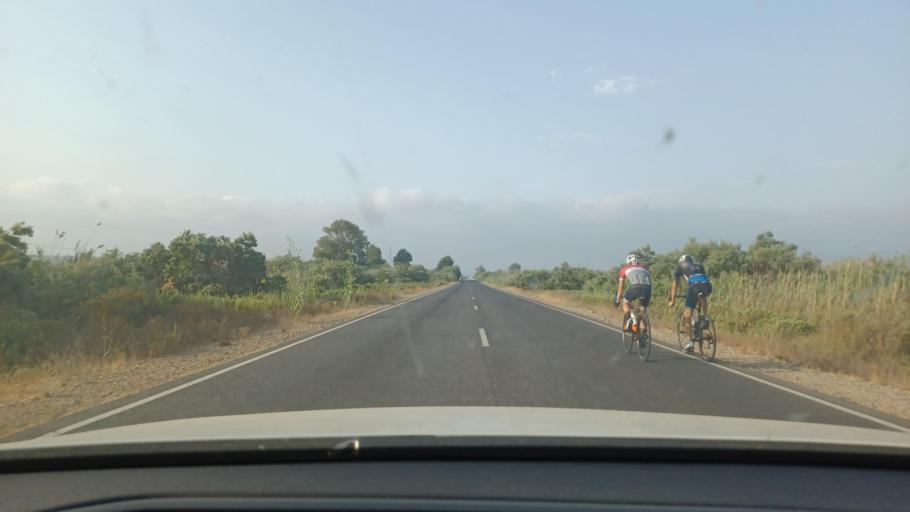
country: ES
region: Valencia
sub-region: Provincia de Alicante
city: Dolores
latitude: 38.1726
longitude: -0.7021
